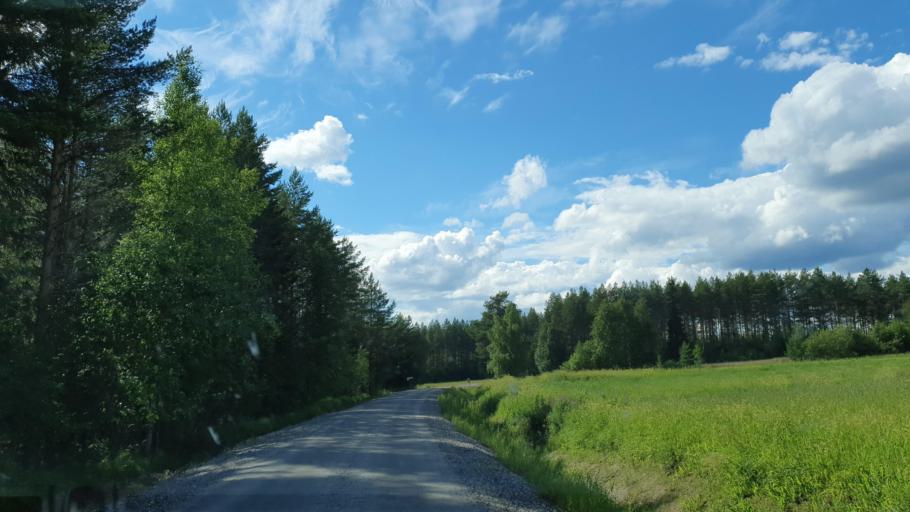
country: FI
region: Kainuu
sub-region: Kehys-Kainuu
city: Kuhmo
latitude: 64.1468
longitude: 29.7565
